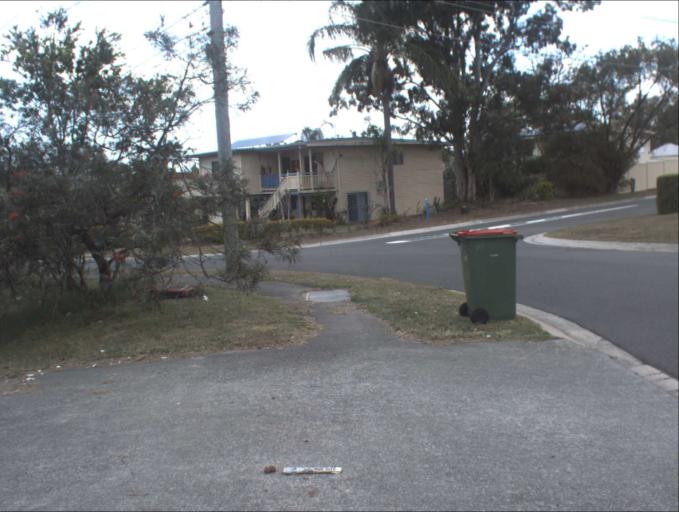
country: AU
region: Queensland
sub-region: Logan
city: Logan City
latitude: -27.6512
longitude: 153.1055
